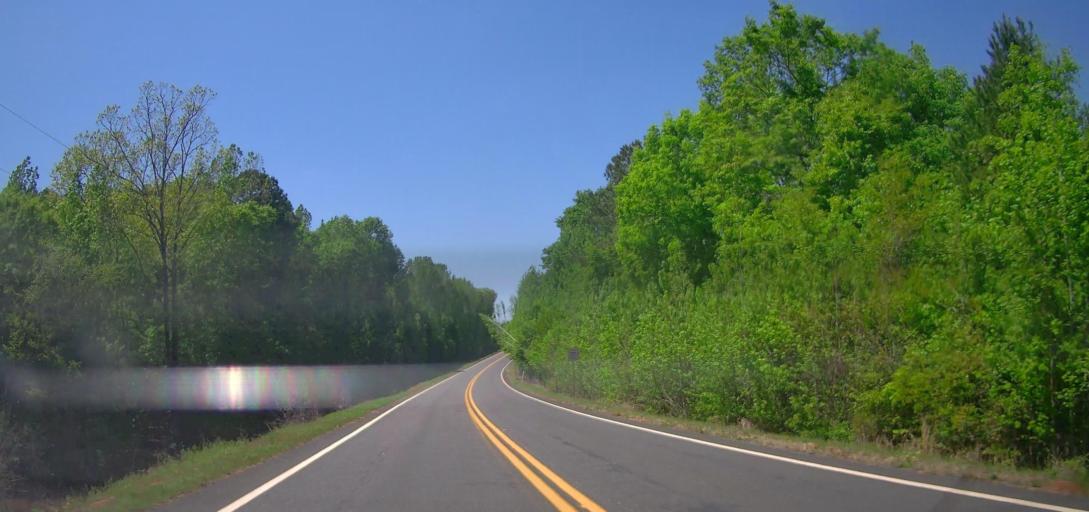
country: US
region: Georgia
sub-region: Jasper County
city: Monticello
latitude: 33.2366
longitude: -83.5480
